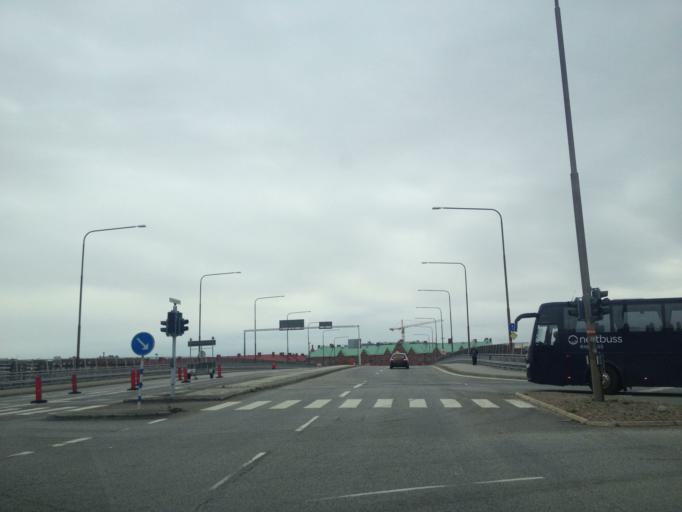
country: SE
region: Skane
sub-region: Malmo
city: Malmoe
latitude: 55.6121
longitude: 13.0180
